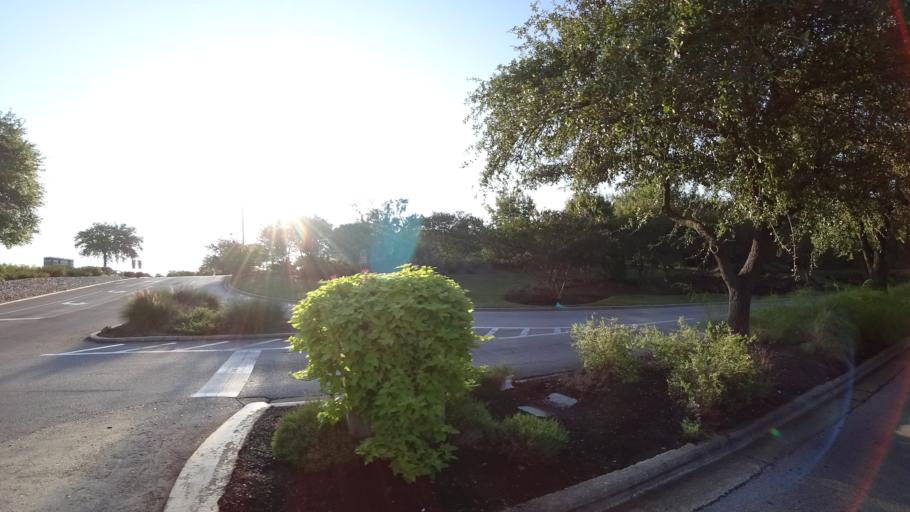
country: US
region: Texas
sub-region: Travis County
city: Rollingwood
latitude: 30.2545
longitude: -97.8081
